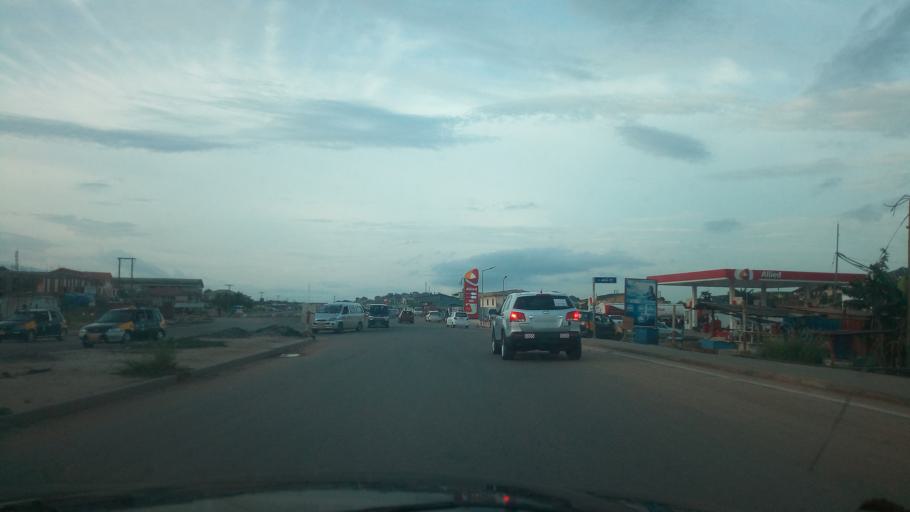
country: GH
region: Western
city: Takoradi
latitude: 4.9228
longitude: -1.7845
